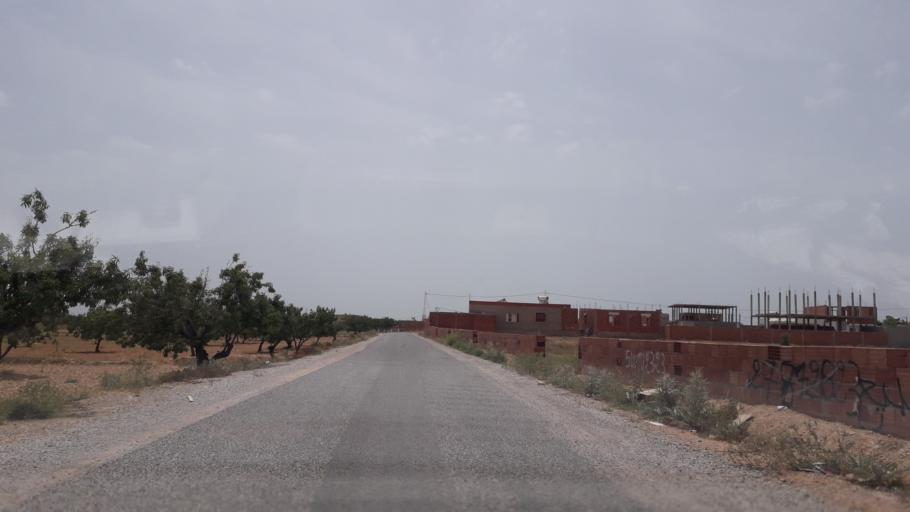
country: TN
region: Safaqis
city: Al Qarmadah
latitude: 34.8469
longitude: 10.7749
